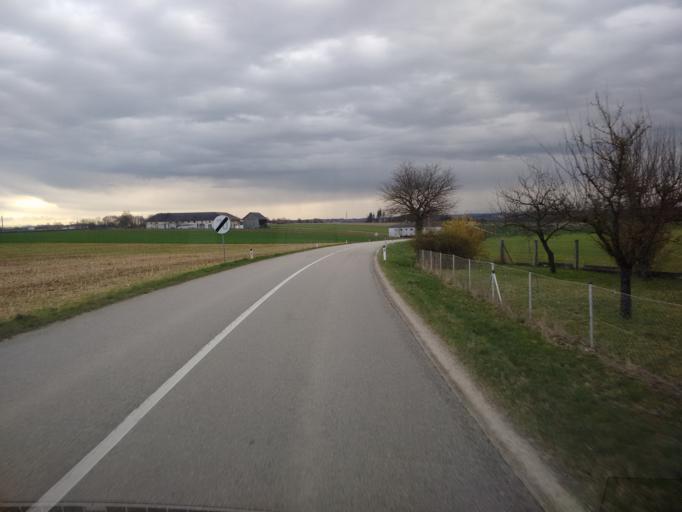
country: AT
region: Upper Austria
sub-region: Politischer Bezirk Linz-Land
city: Horsching
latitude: 48.1492
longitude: 14.1988
